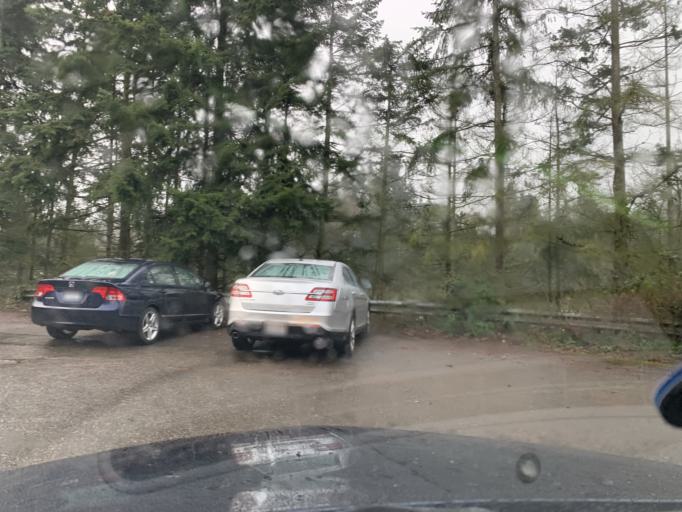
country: US
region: Washington
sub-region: King County
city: Mercer Island
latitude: 47.5821
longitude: -122.2180
